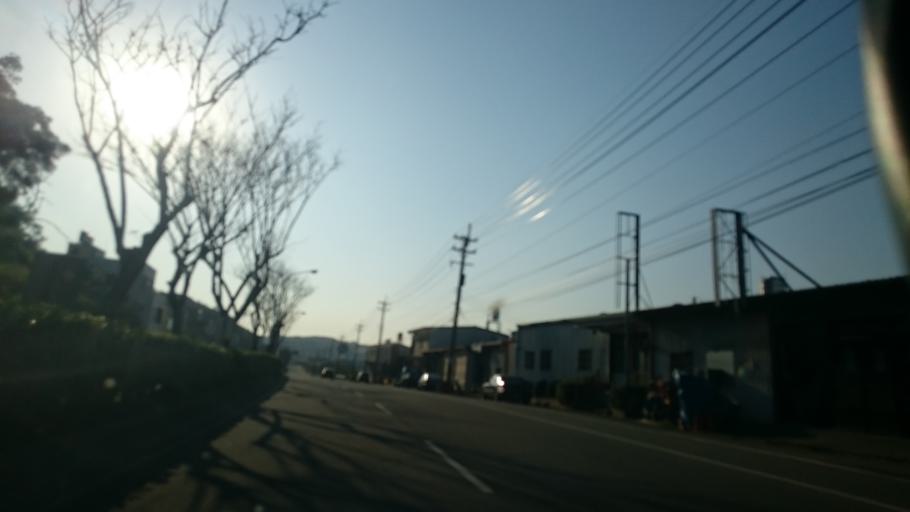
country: TW
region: Taiwan
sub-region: Miaoli
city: Miaoli
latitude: 24.6575
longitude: 120.8618
